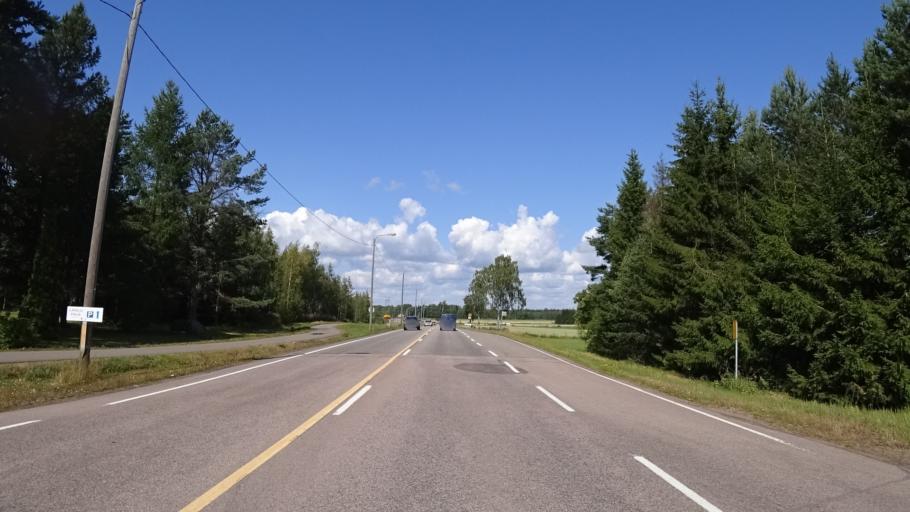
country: FI
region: Kymenlaakso
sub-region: Kotka-Hamina
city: Karhula
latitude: 60.5333
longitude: 26.9369
